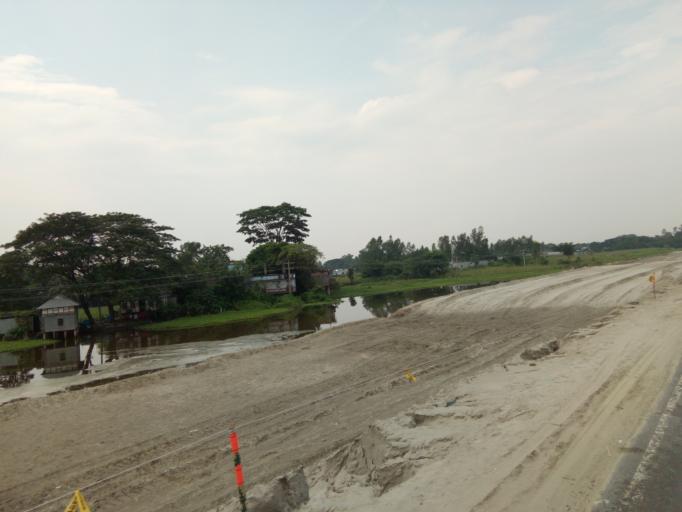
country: BD
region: Dhaka
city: Dohar
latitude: 23.5372
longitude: 90.2918
